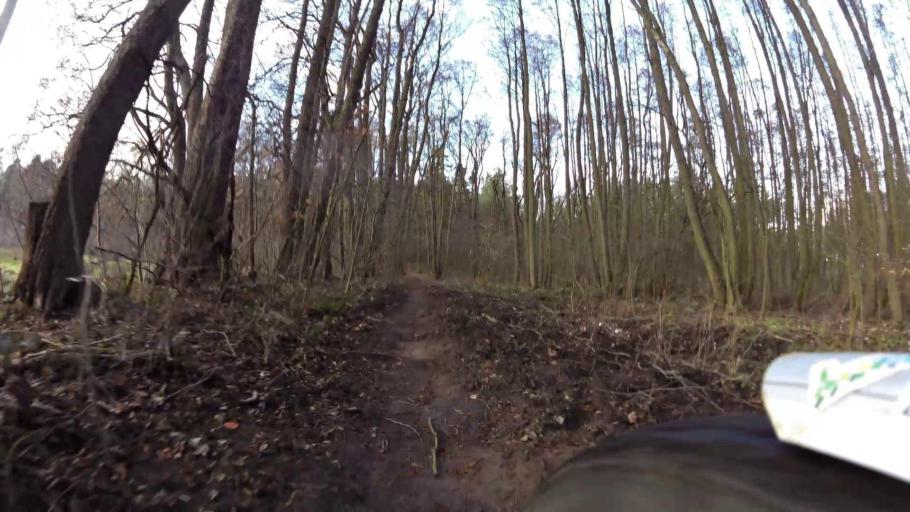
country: PL
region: West Pomeranian Voivodeship
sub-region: Powiat kamienski
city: Wolin
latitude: 53.8475
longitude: 14.7057
